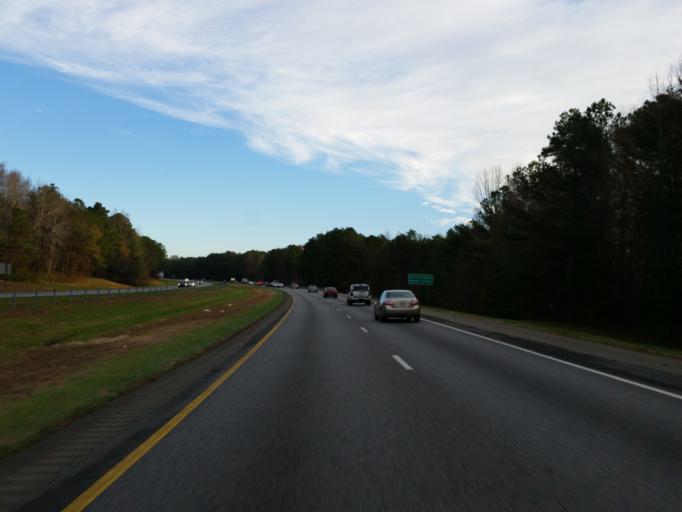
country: US
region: Georgia
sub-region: Cherokee County
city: Holly Springs
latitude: 34.2011
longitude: -84.4969
